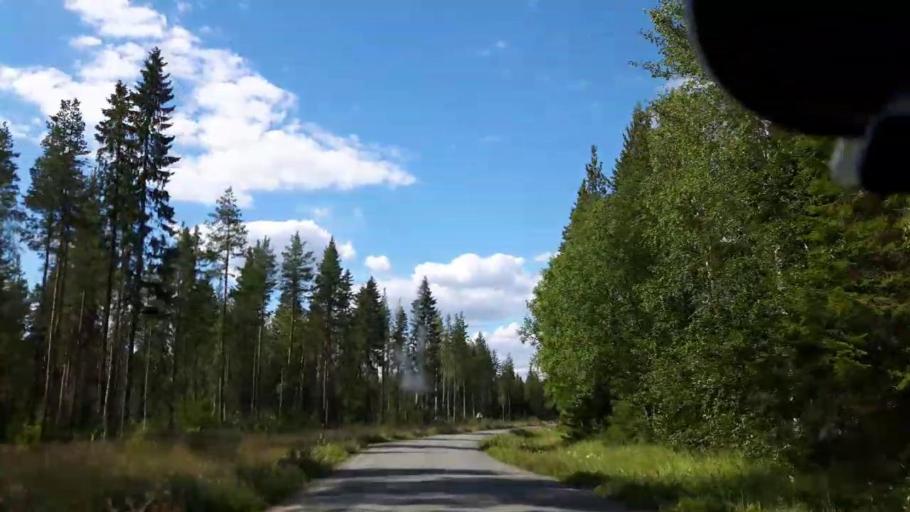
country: SE
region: Jaemtland
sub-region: Braecke Kommun
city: Braecke
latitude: 62.8407
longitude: 15.2994
